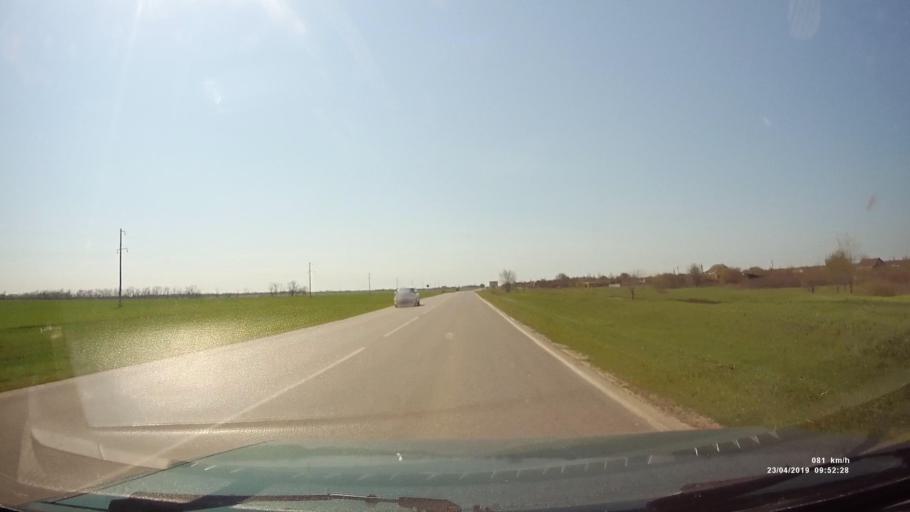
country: RU
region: Rostov
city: Orlovskiy
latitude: 46.8441
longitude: 42.0459
